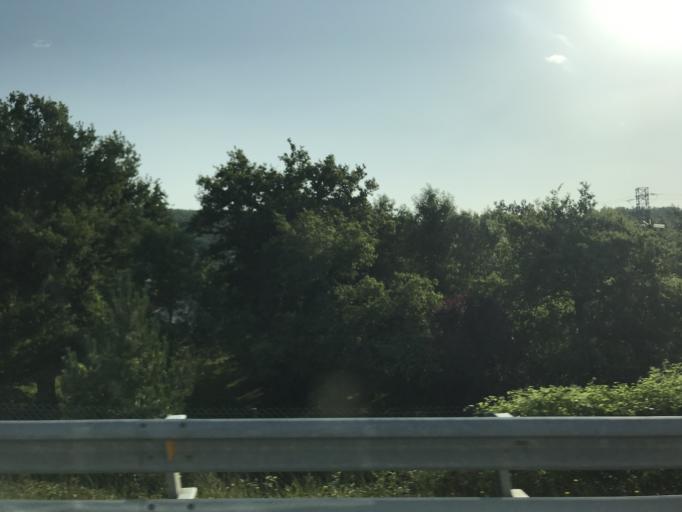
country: ES
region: Navarre
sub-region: Provincia de Navarra
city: Altsasu
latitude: 42.9116
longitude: -2.1785
